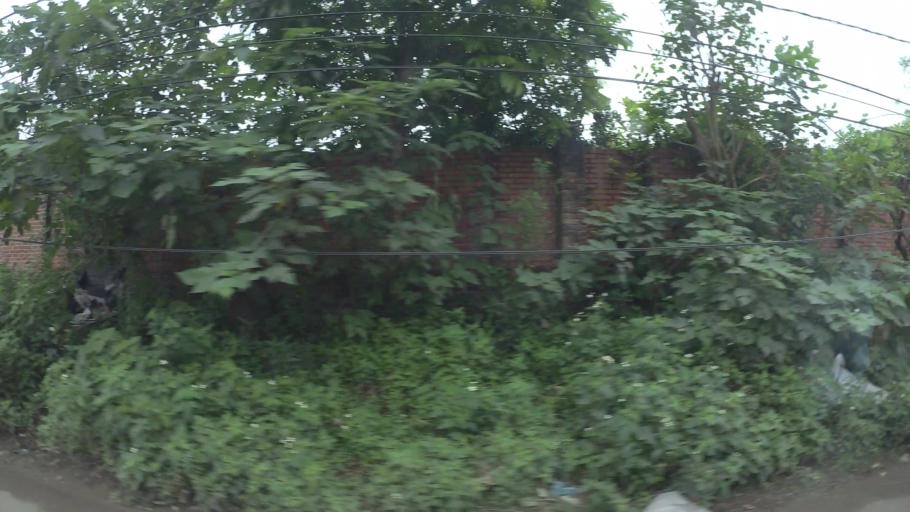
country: VN
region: Ha Noi
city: Tay Ho
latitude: 21.0596
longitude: 105.8388
